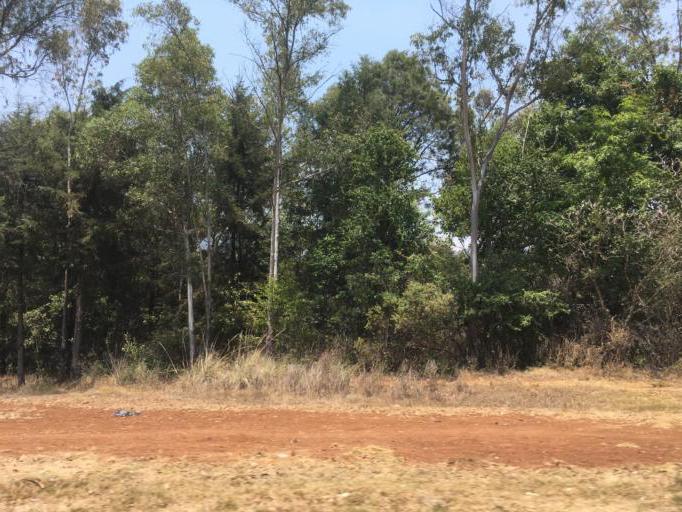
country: MX
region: Michoacan
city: Quiroga
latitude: 19.6533
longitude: -101.4948
